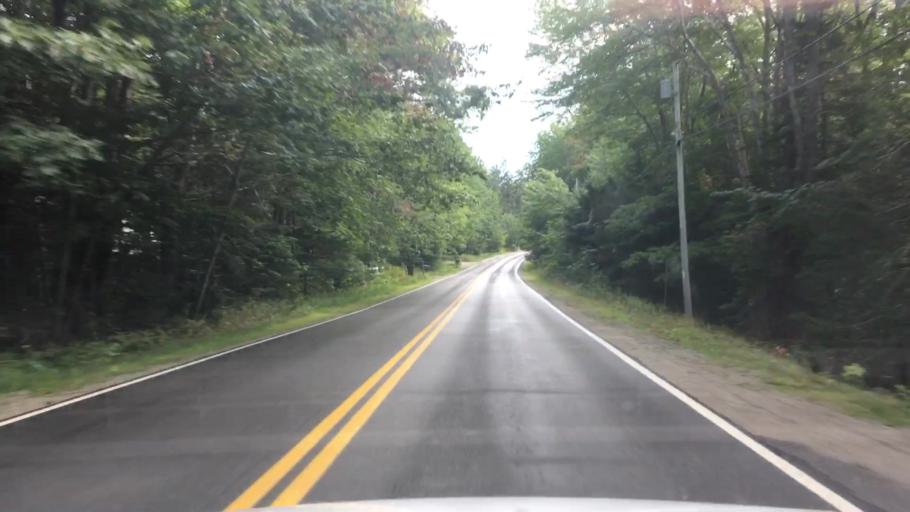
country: US
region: Maine
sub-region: Hancock County
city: Trenton
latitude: 44.4628
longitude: -68.4242
